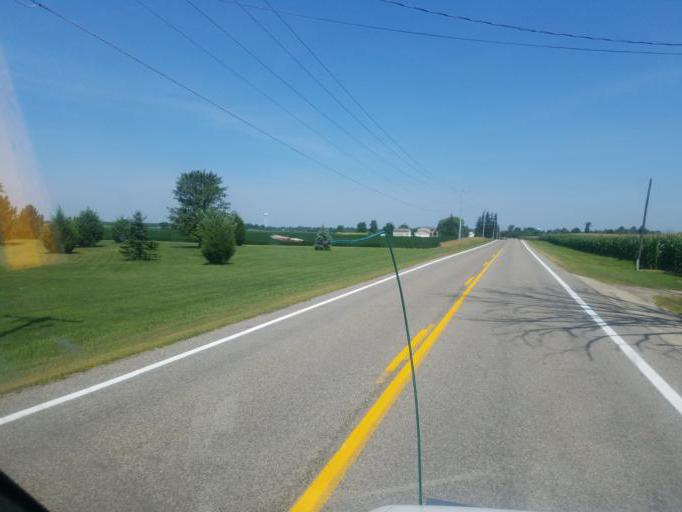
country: US
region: Ohio
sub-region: Champaign County
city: North Lewisburg
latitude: 40.2088
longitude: -83.5399
